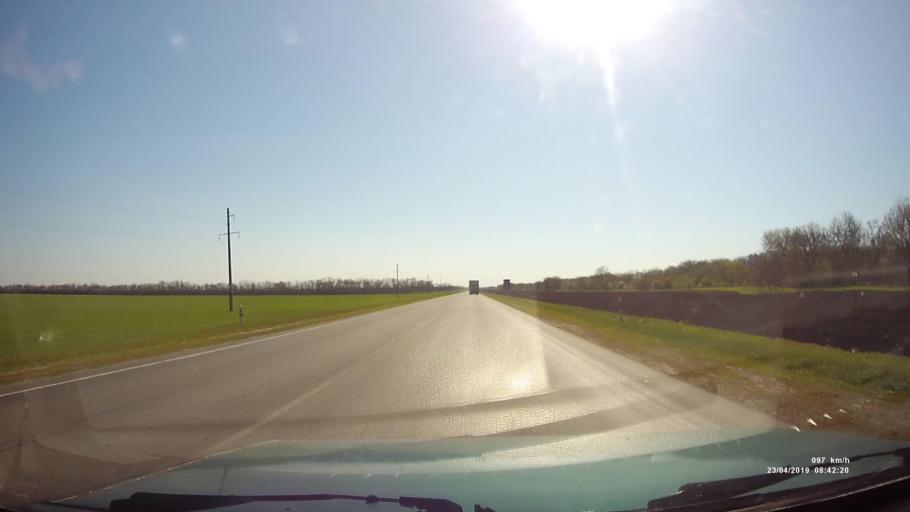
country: RU
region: Rostov
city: Gigant
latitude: 46.5238
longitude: 41.2679
